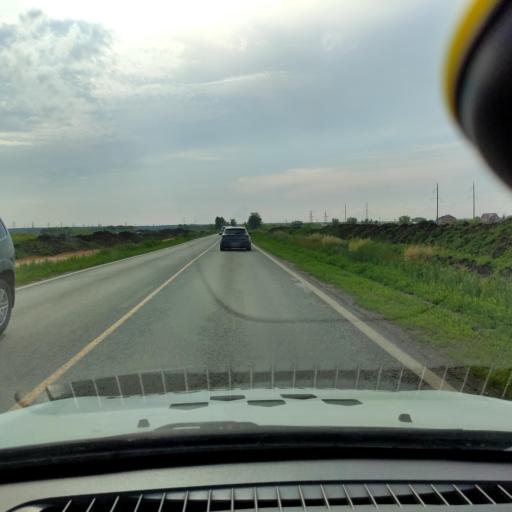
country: RU
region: Samara
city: Podstepki
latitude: 53.5689
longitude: 49.1105
